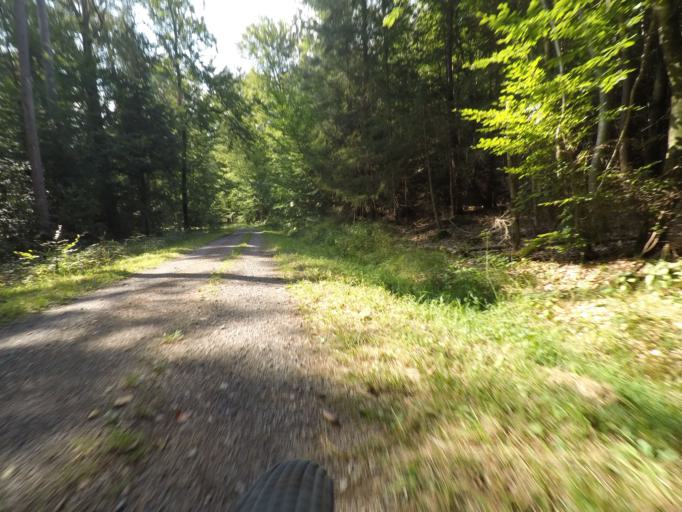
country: DE
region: Baden-Wuerttemberg
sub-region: Regierungsbezirk Stuttgart
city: Steinenbronn
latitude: 48.6820
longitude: 9.1041
